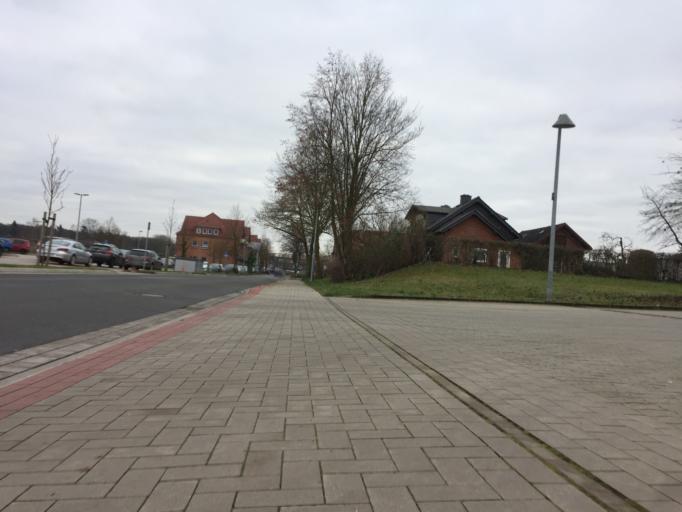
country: DE
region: Lower Saxony
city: Sulingen
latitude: 52.6863
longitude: 8.8129
